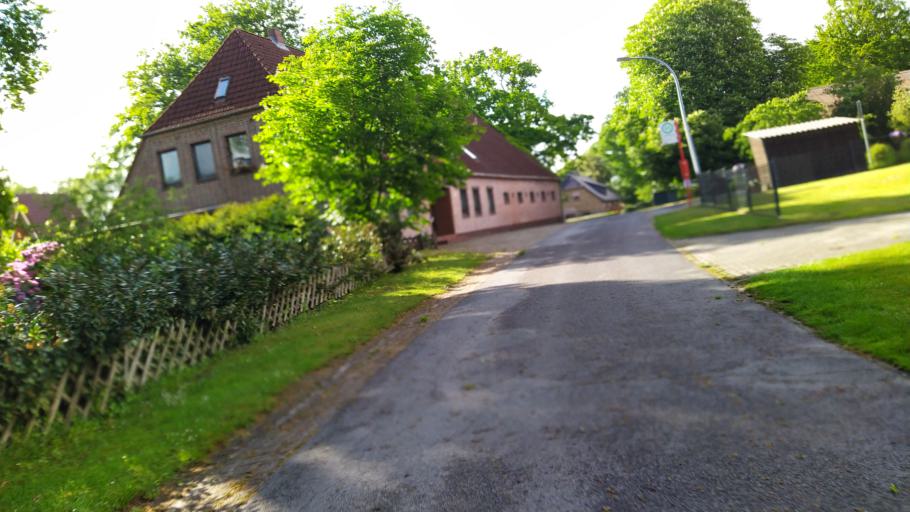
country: DE
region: Lower Saxony
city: Farven
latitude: 53.4397
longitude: 9.3451
